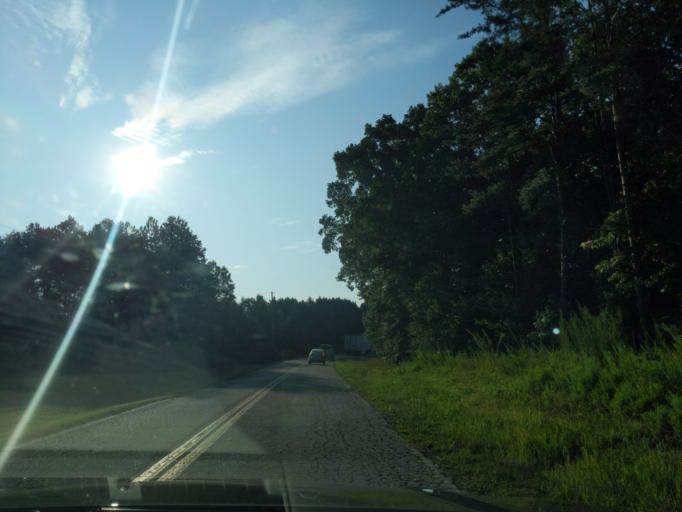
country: US
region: South Carolina
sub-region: Spartanburg County
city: Roebuck
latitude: 34.7986
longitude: -81.9763
